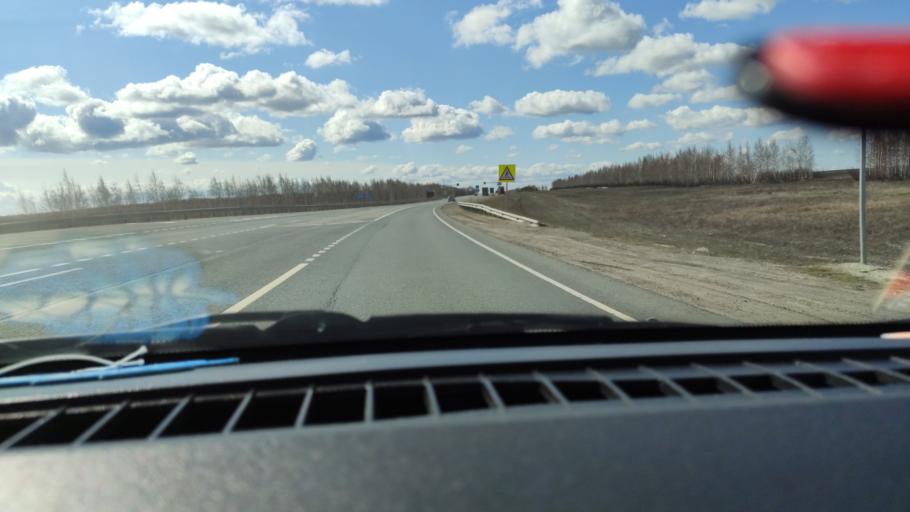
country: RU
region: Samara
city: Syzran'
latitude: 52.9505
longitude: 48.3058
